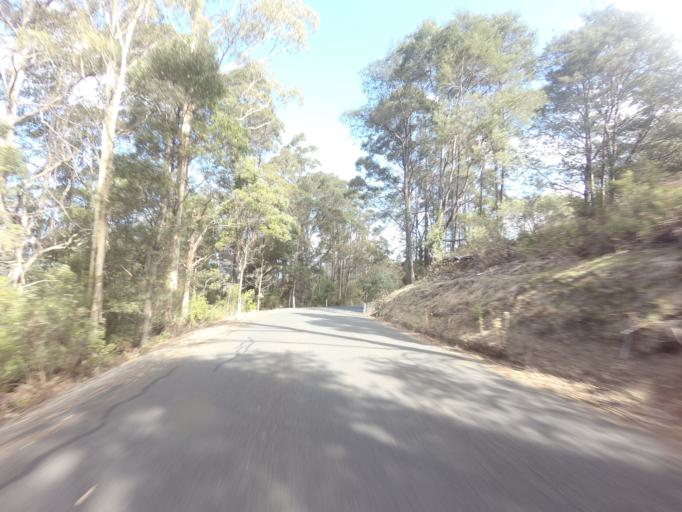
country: AU
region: Tasmania
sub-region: Break O'Day
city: St Helens
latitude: -41.6527
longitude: 148.2467
